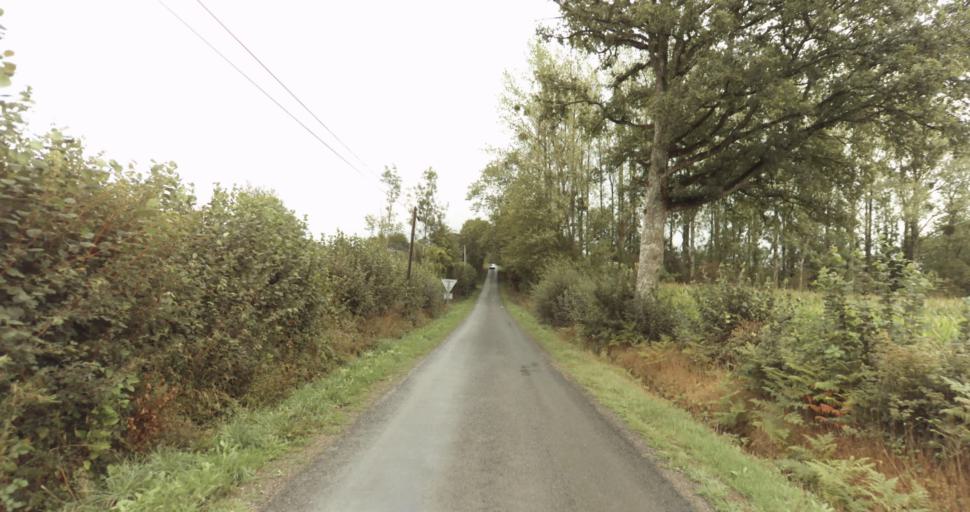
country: FR
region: Lower Normandy
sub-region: Departement de l'Orne
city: Sainte-Gauburge-Sainte-Colombe
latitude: 48.6905
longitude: 0.4130
